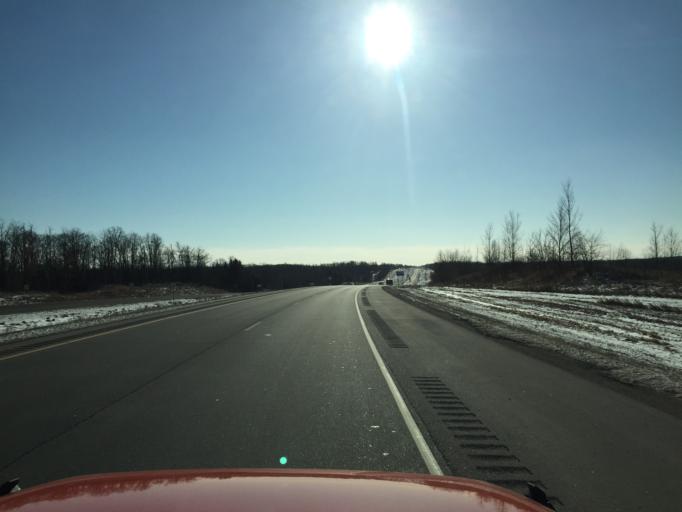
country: US
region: Minnesota
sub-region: Mille Lacs County
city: Milaca
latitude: 45.8218
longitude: -93.6558
